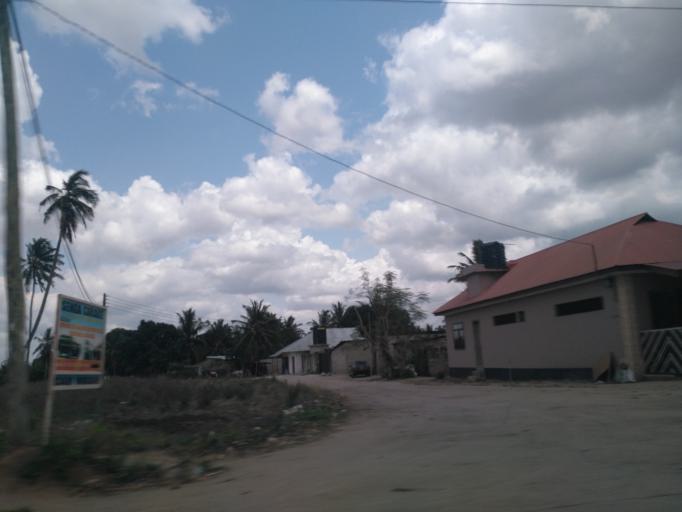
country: TZ
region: Dar es Salaam
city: Dar es Salaam
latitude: -6.8709
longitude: 39.3470
